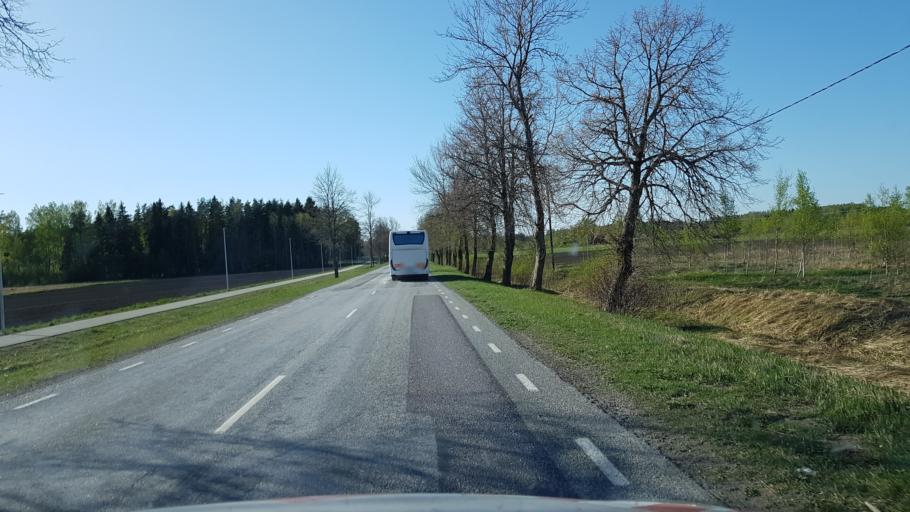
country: EE
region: Paernumaa
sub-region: Paikuse vald
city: Paikuse
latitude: 58.3623
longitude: 24.6498
